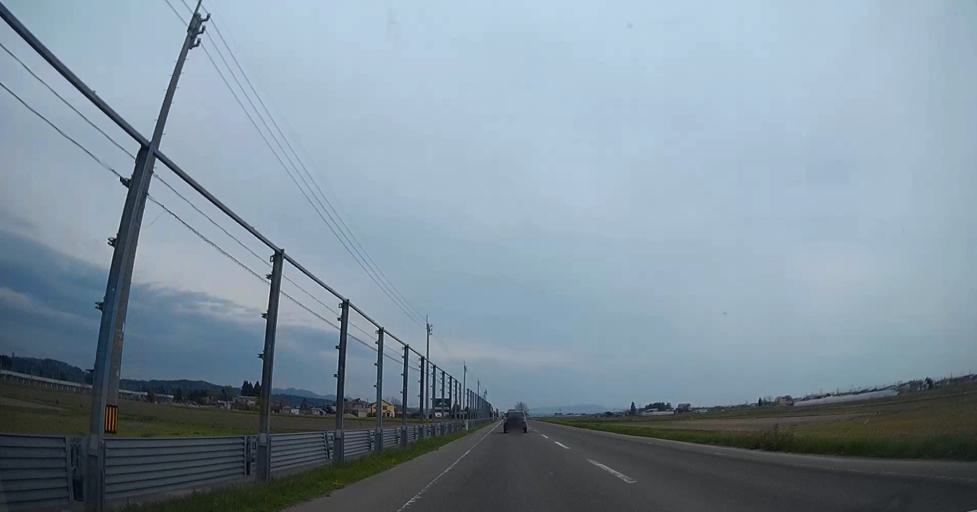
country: JP
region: Aomori
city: Aomori Shi
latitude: 40.8655
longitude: 140.6795
